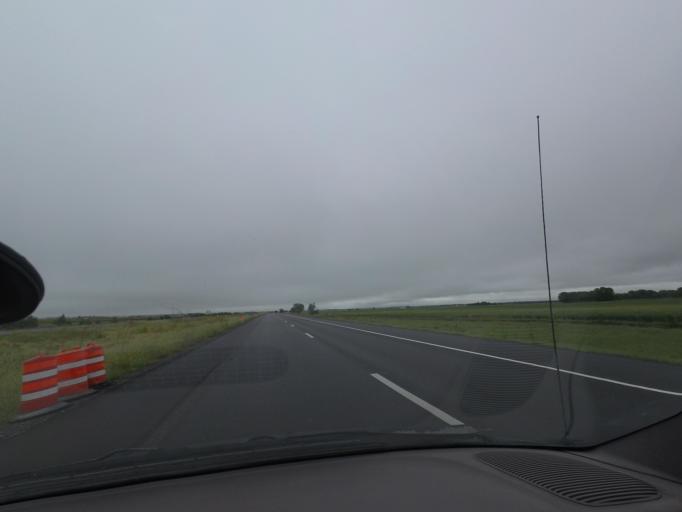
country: US
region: Illinois
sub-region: Macon County
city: Harristown
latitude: 39.8311
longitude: -89.1366
